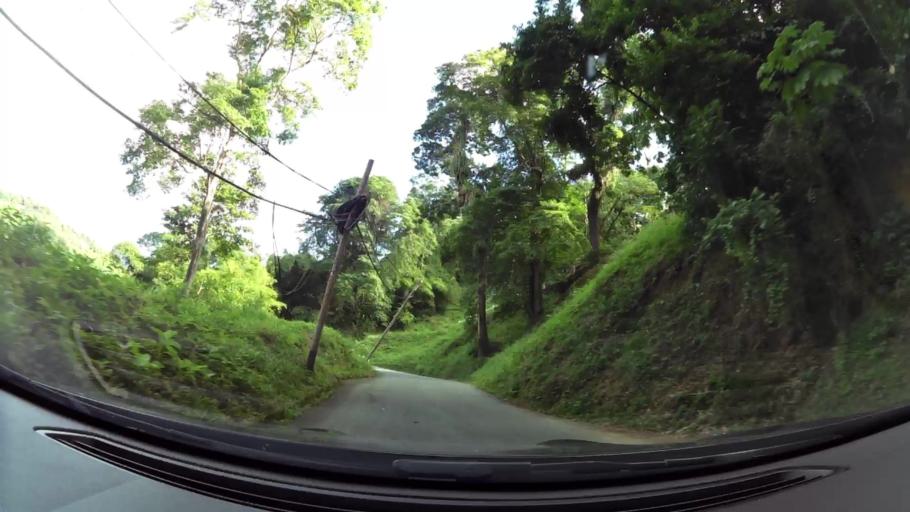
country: TT
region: Eastern Tobago
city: Roxborough
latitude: 11.3206
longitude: -60.5482
